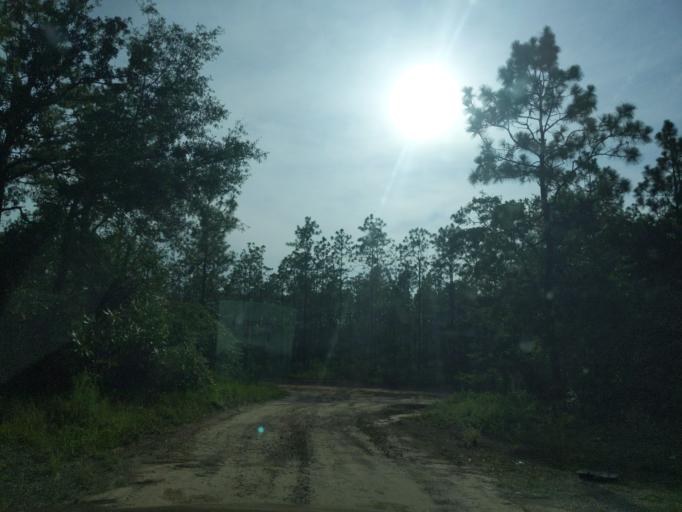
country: US
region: Florida
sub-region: Gadsden County
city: Midway
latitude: 30.3924
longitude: -84.4093
